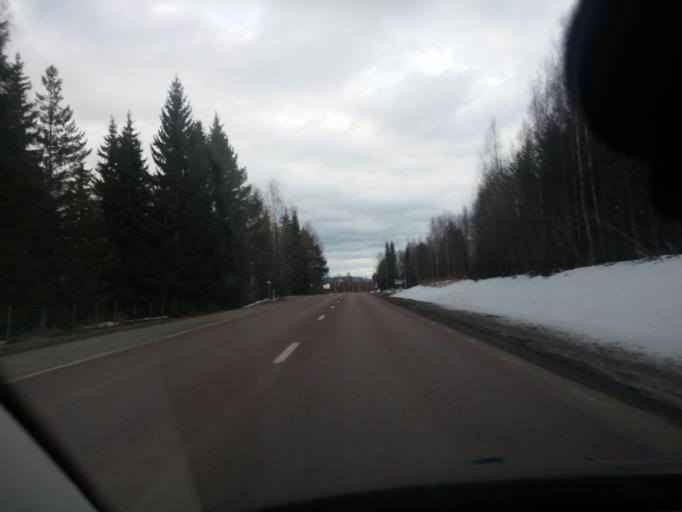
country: SE
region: Gaevleborg
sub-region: Ljusdals Kommun
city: Ljusdal
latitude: 61.8165
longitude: 16.0754
